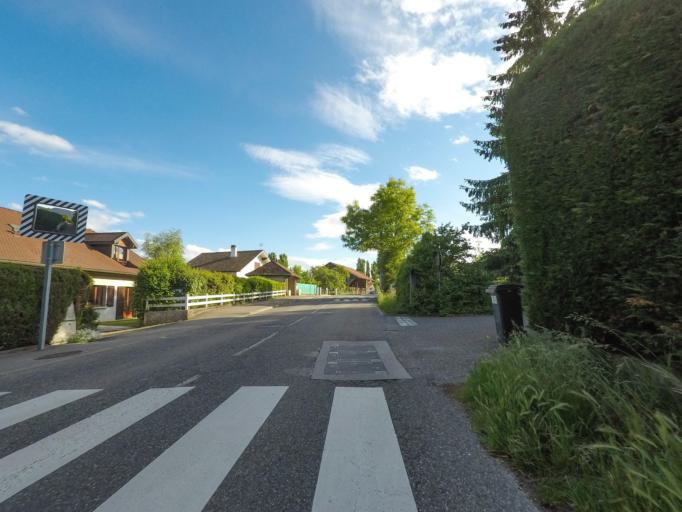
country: FR
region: Rhone-Alpes
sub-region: Departement de l'Ain
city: Saint-Genis-Pouilly
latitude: 46.2530
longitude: 6.0346
